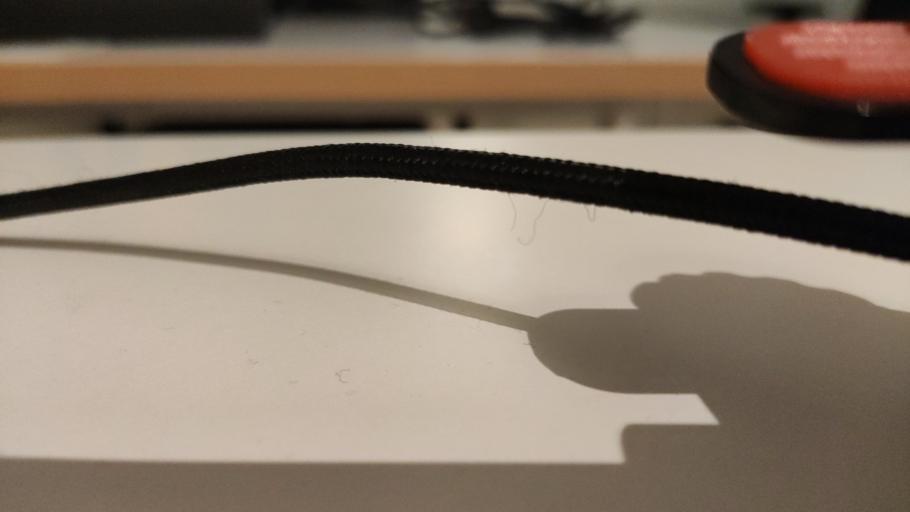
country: RU
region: Moskovskaya
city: Gorshkovo
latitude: 56.3738
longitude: 37.4133
